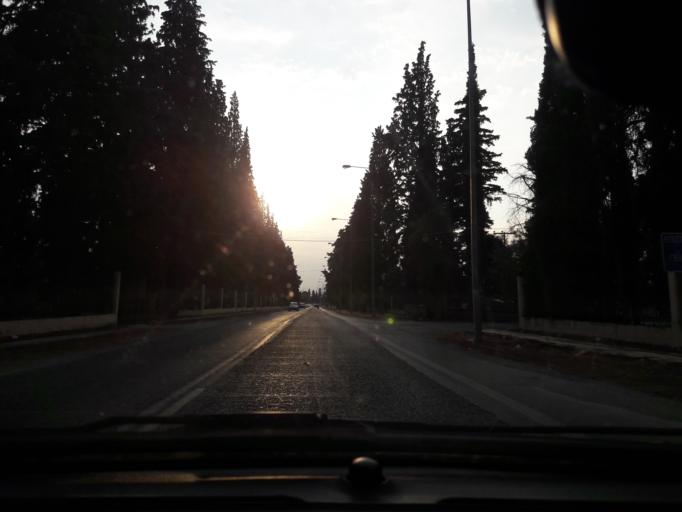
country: GR
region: Central Macedonia
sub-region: Nomos Thessalonikis
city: Thermi
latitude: 40.5391
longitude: 22.9968
